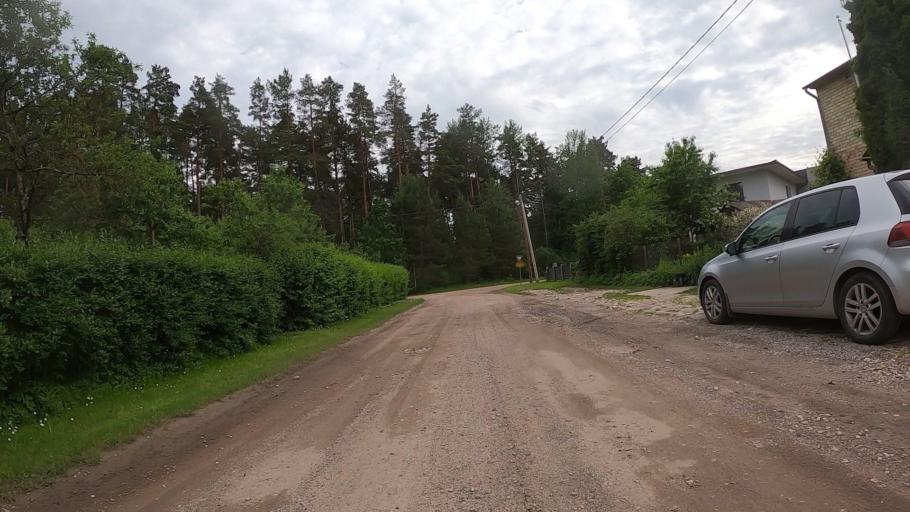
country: LV
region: Ozolnieku
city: Ozolnieki
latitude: 56.6897
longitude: 23.7678
